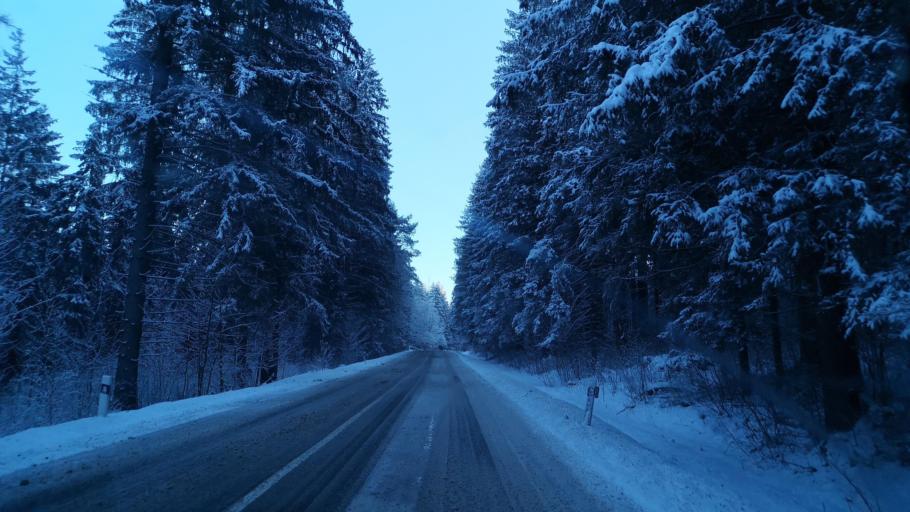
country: SK
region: Banskobystricky
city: Revuca
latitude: 48.8283
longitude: 20.1151
